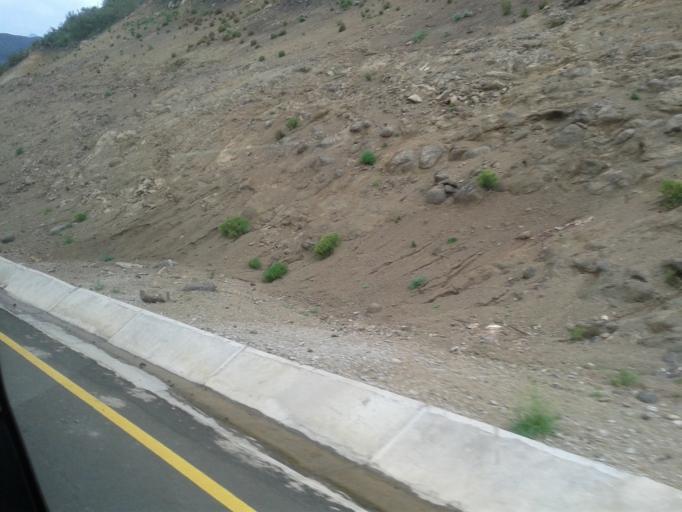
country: LS
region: Maseru
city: Nako
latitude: -29.6560
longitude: 27.8498
